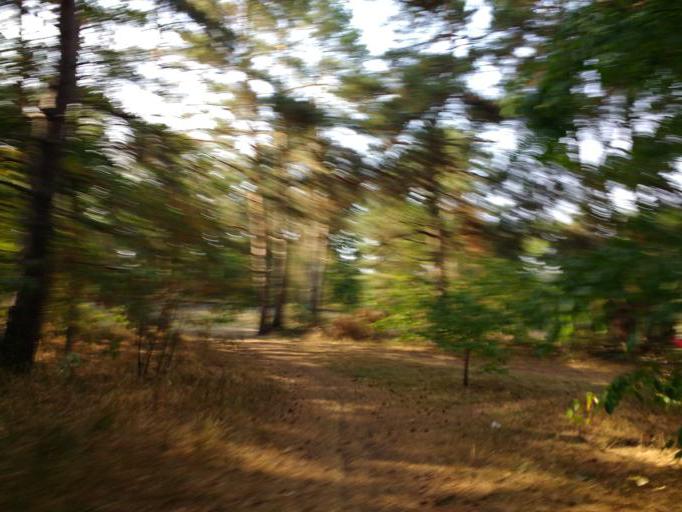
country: DE
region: Lower Saxony
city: Gifhorn
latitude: 52.4701
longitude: 10.5343
